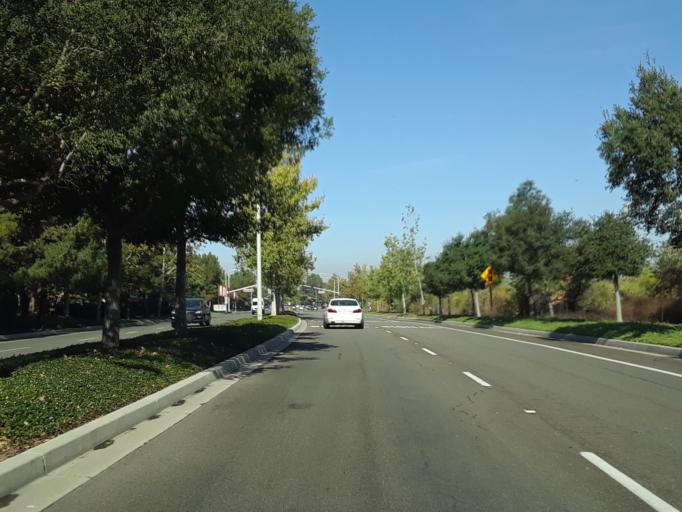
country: US
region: California
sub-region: Orange County
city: Irvine
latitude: 33.6713
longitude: -117.7809
